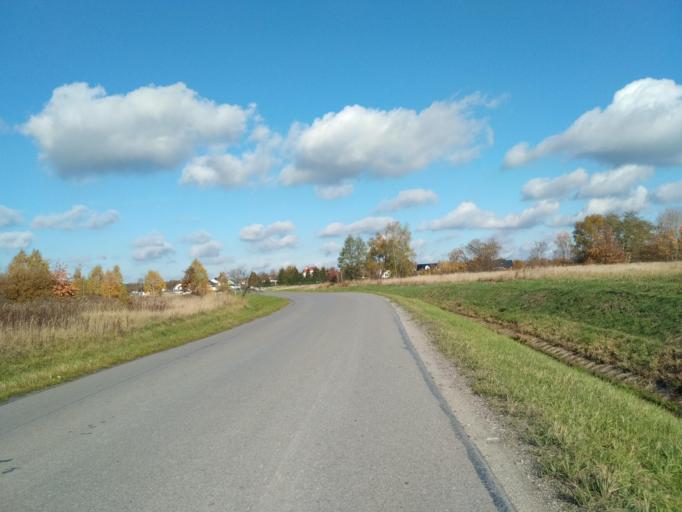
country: PL
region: Subcarpathian Voivodeship
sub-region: Powiat rzeszowski
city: Swilcza
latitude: 50.1292
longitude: 21.9028
